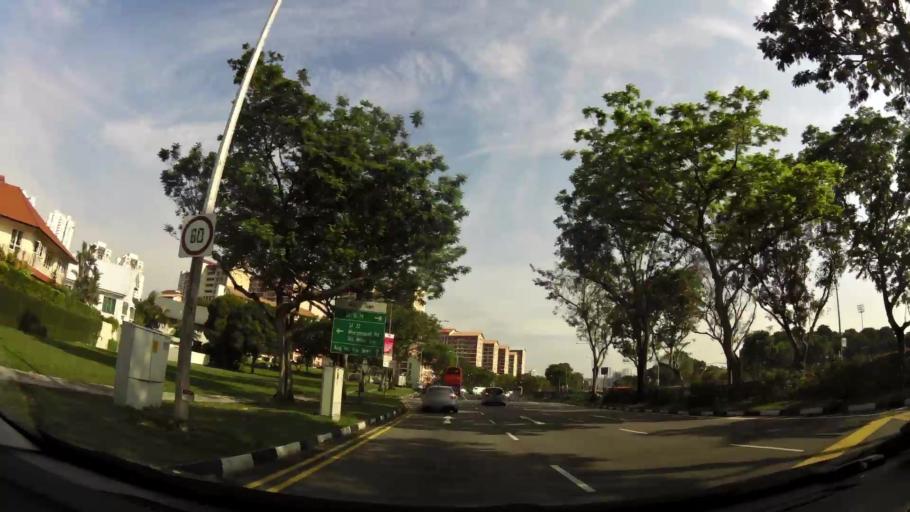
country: SG
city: Singapore
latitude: 1.3527
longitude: 103.8481
